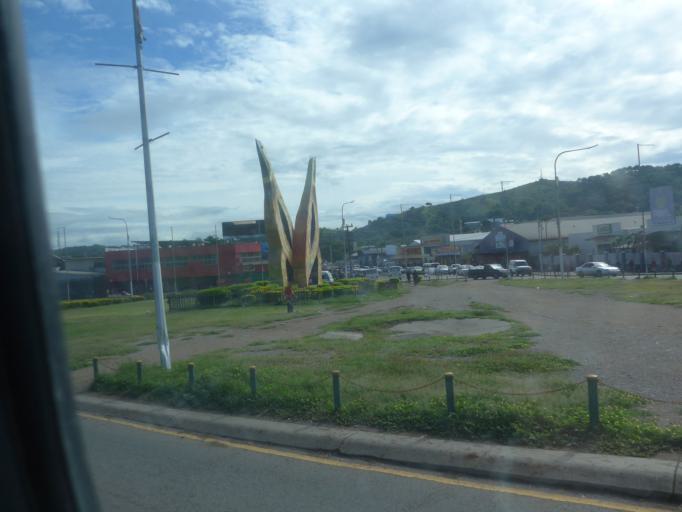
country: PG
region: National Capital
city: Port Moresby
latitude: -9.4637
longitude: 147.1947
